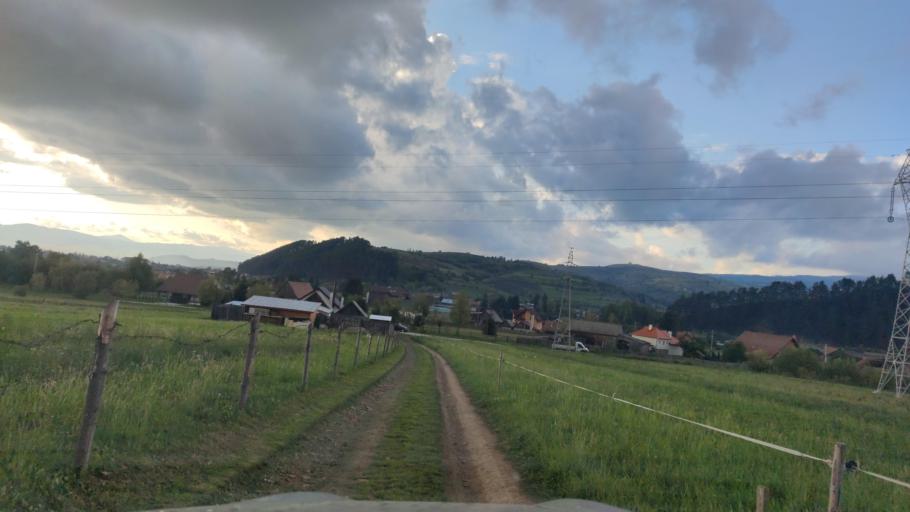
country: RO
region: Harghita
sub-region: Municipiul Gheorgheni
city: Gheorgheni
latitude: 46.7221
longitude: 25.6357
